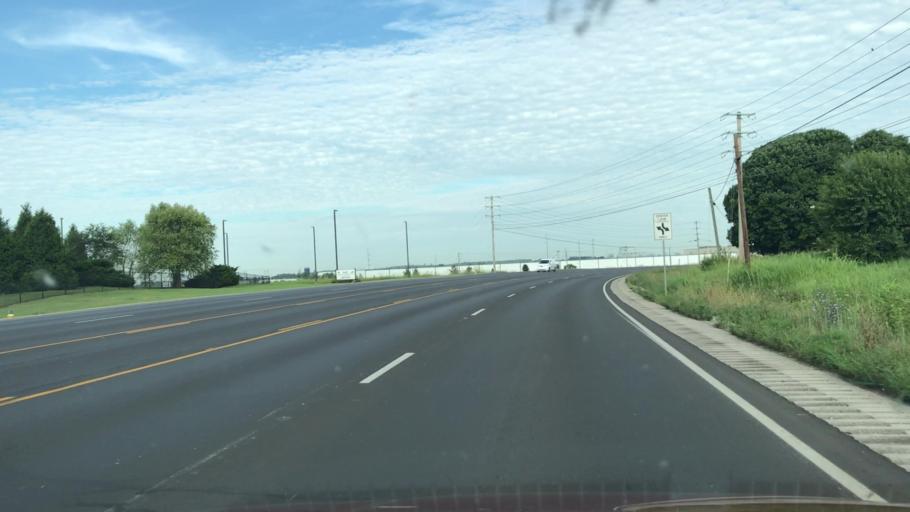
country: US
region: Kentucky
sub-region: Warren County
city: Bowling Green
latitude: 37.0333
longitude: -86.3252
